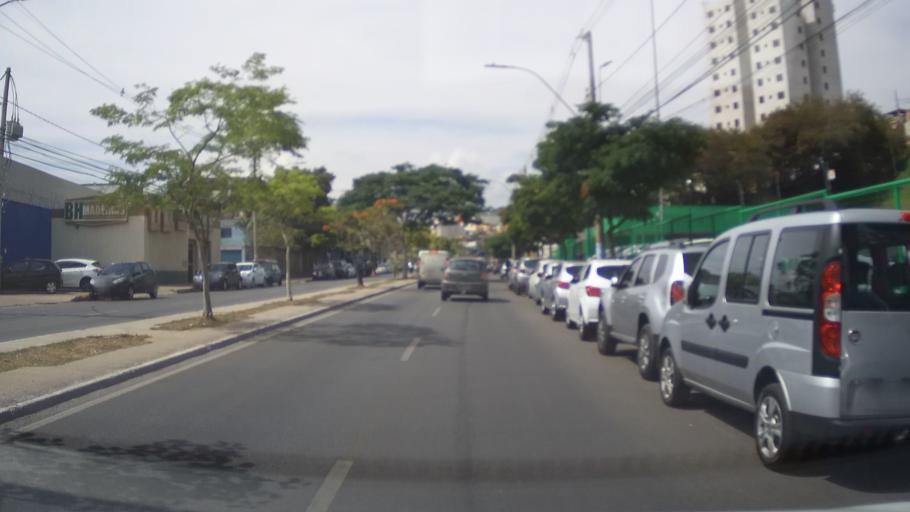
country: BR
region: Minas Gerais
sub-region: Belo Horizonte
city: Belo Horizonte
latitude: -19.9457
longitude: -43.9695
